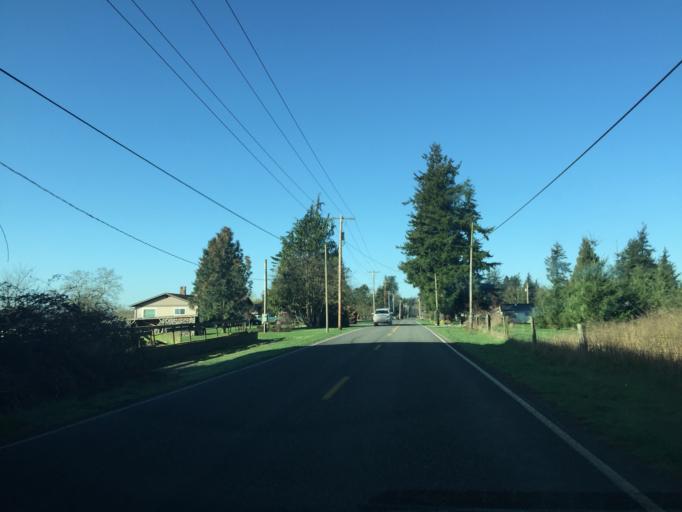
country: US
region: Washington
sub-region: Whatcom County
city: Lynden
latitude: 48.9065
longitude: -122.4943
